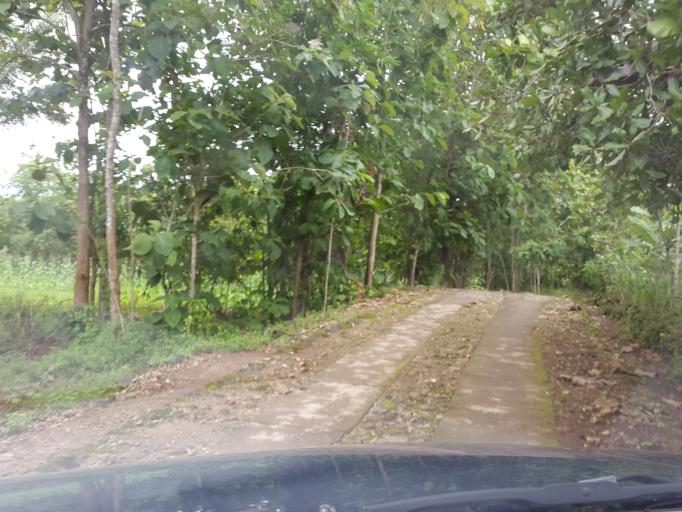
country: ID
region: Daerah Istimewa Yogyakarta
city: Wonosari
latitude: -7.9254
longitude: 110.6809
